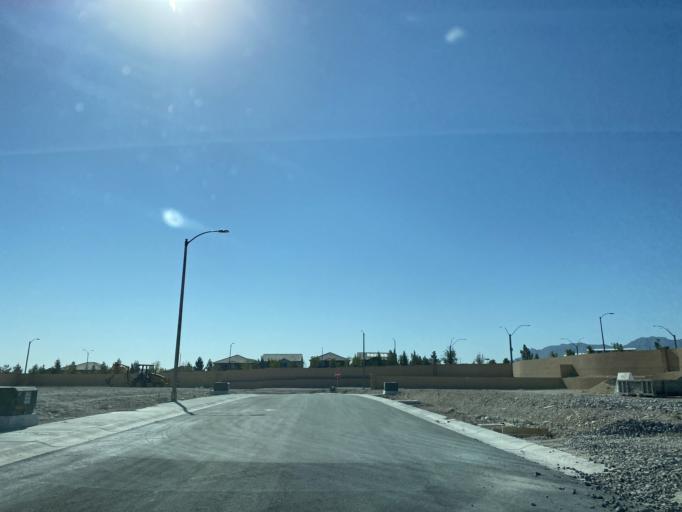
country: US
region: Nevada
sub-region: Clark County
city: Summerlin South
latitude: 36.3156
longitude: -115.3142
